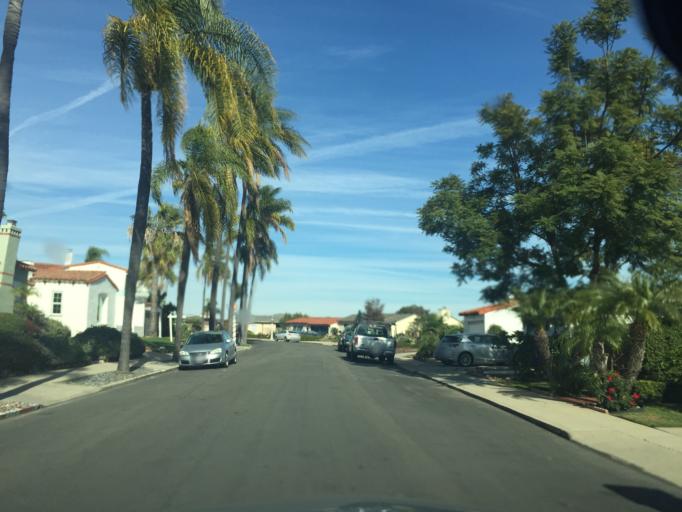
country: US
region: California
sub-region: San Diego County
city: Lemon Grove
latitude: 32.7666
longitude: -117.0984
